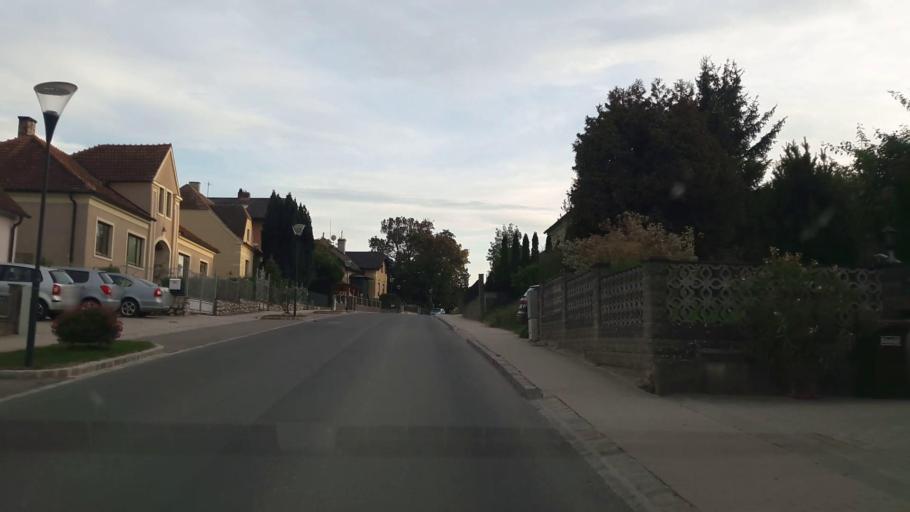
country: AT
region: Lower Austria
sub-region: Politischer Bezirk Korneuburg
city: Ernstbrunn
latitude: 48.5316
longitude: 16.3618
